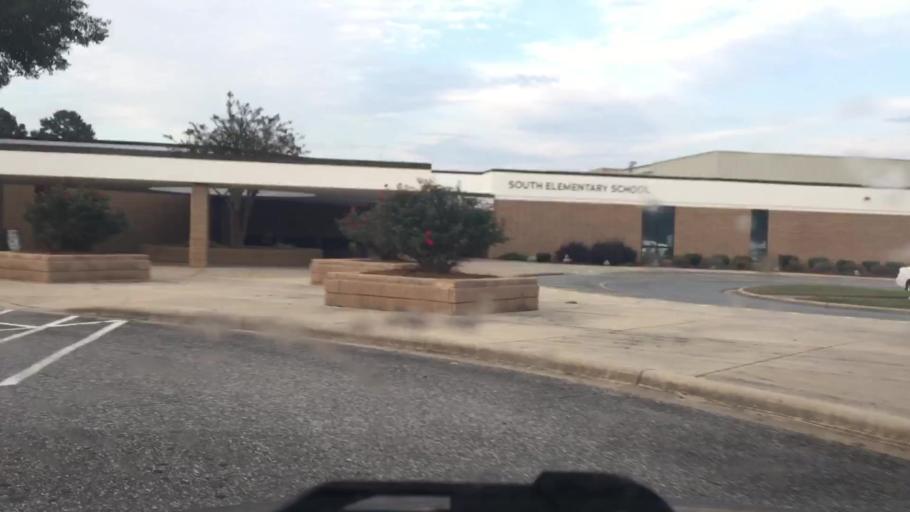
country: US
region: North Carolina
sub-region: Iredell County
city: Mooresville
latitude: 35.5628
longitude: -80.8024
